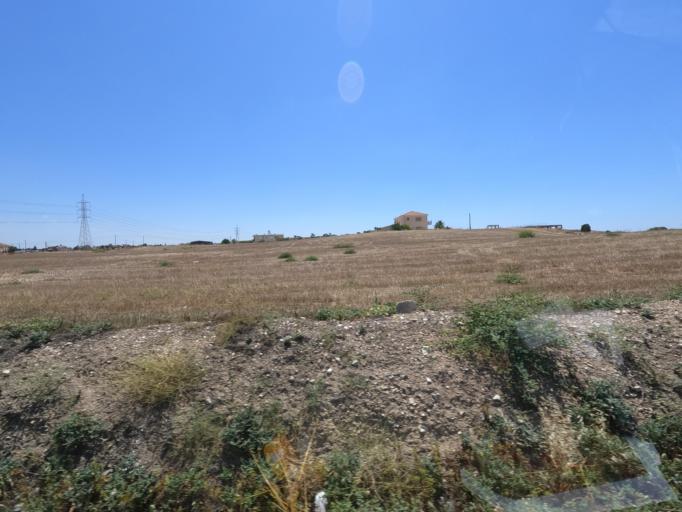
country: CY
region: Larnaka
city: Pyla
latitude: 35.0024
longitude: 33.6884
